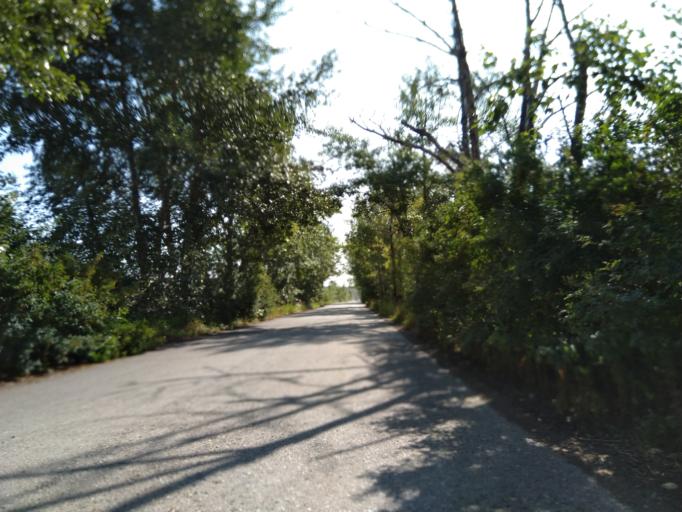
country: CA
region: Alberta
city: Calgary
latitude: 51.1019
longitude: -114.2222
